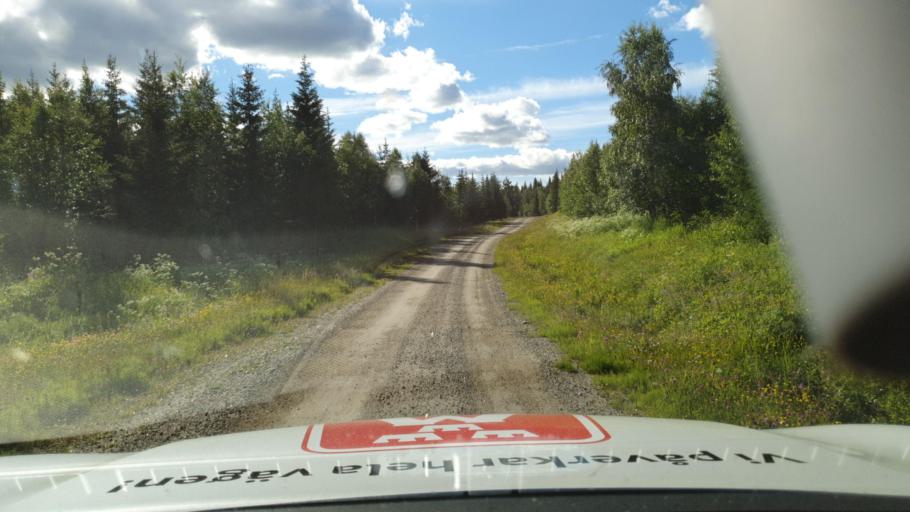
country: SE
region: Vaesterbotten
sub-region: Lycksele Kommun
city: Lycksele
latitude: 64.4034
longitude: 18.3051
